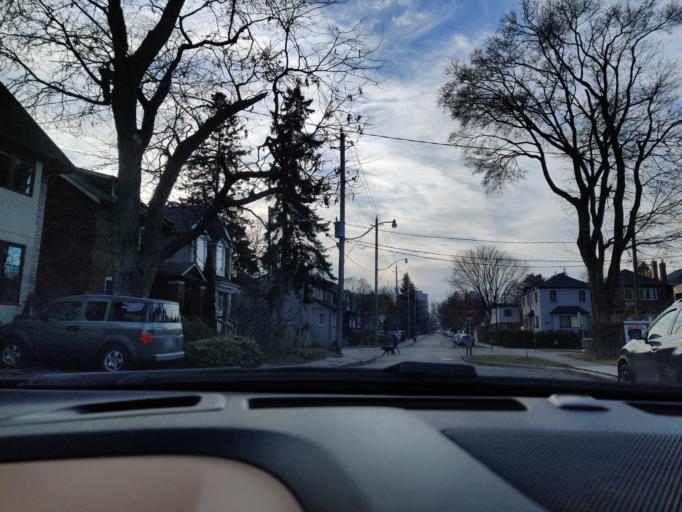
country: CA
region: Ontario
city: Toronto
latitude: 43.7013
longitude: -79.3771
